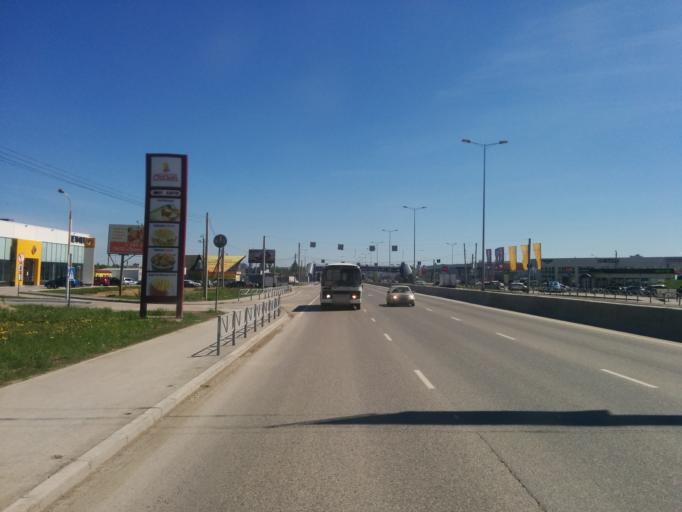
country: RU
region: Perm
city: Perm
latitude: 58.0366
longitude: 56.1962
